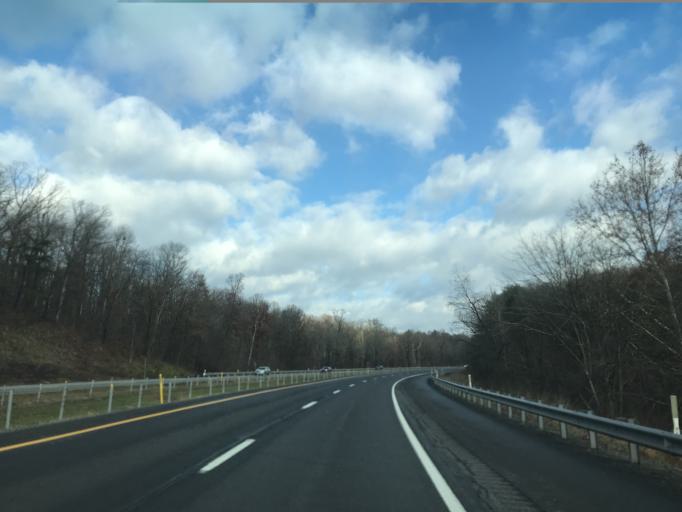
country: US
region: Maryland
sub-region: Washington County
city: Hancock
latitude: 39.8095
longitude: -78.2727
